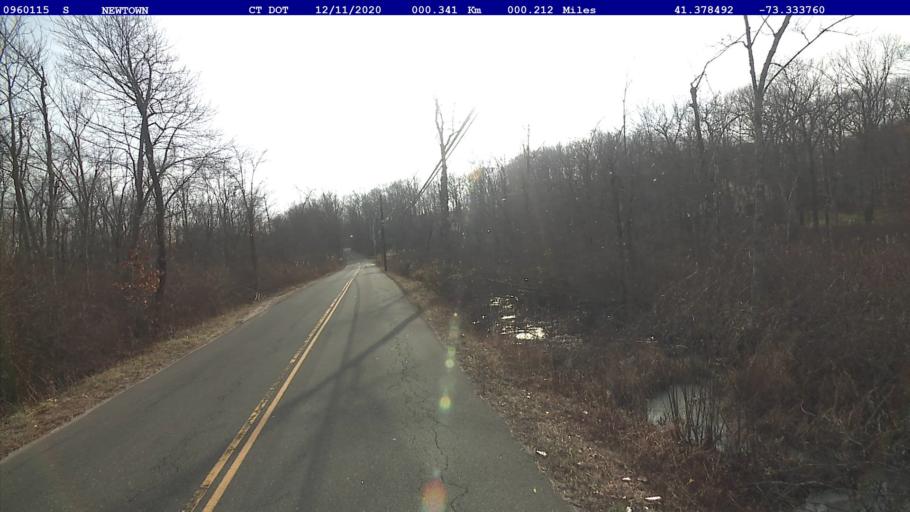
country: US
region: Connecticut
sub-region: Fairfield County
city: Newtown
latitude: 41.3785
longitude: -73.3338
